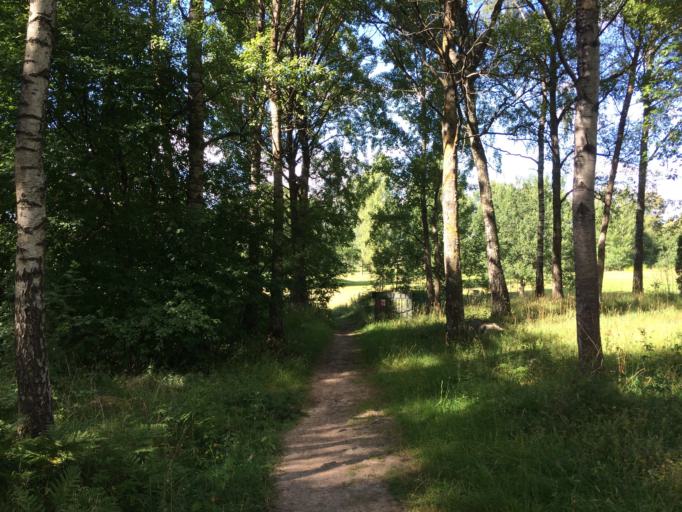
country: SE
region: Stockholm
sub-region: Upplands Vasby Kommun
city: Upplands Vaesby
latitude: 59.4660
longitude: 17.9072
